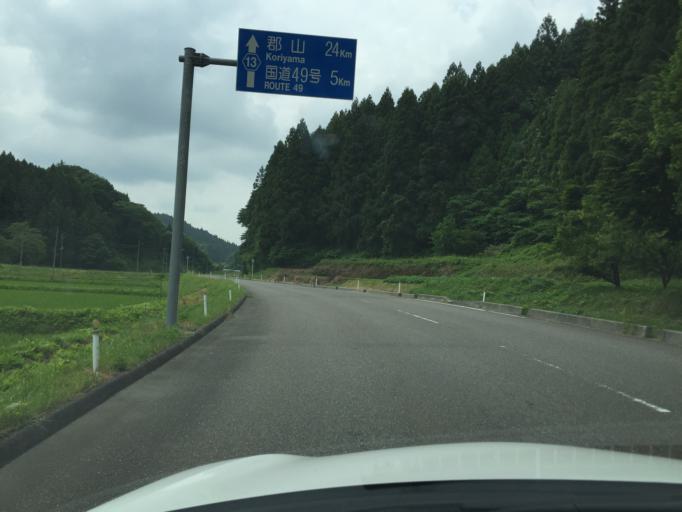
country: JP
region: Fukushima
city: Funehikimachi-funehiki
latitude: 37.2973
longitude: 140.5687
